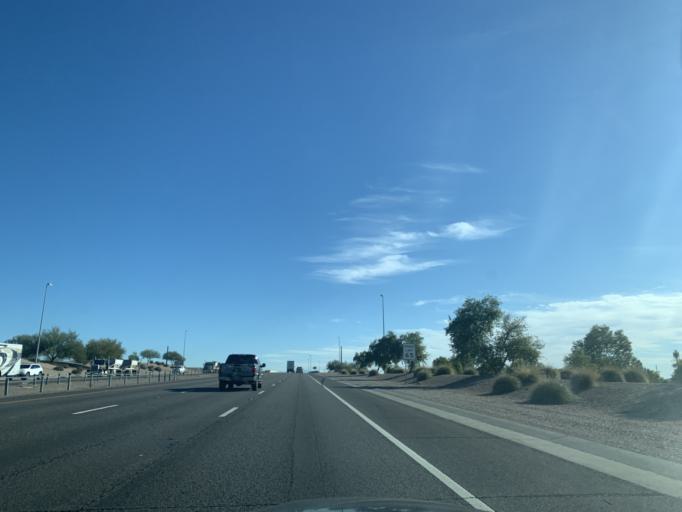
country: US
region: Arizona
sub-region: Maricopa County
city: Chandler
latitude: 33.2827
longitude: -111.7773
